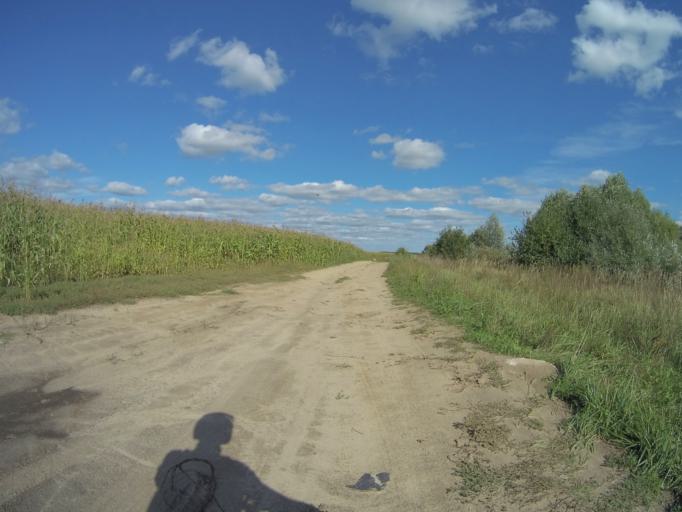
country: RU
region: Vladimir
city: Orgtrud
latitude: 56.3104
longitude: 40.6409
